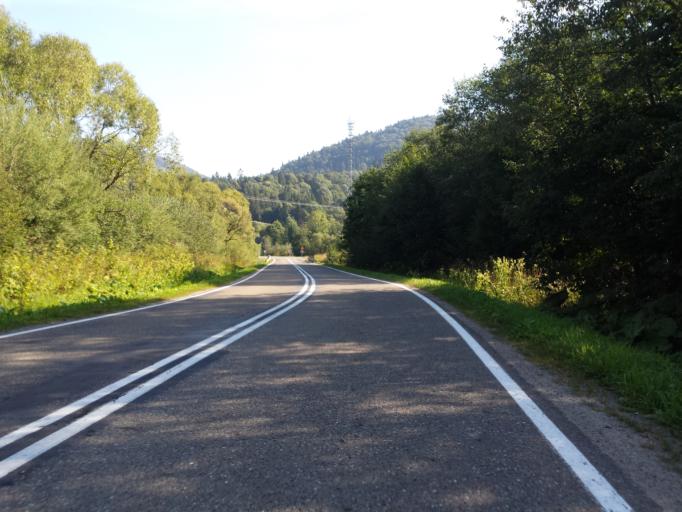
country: PL
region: Subcarpathian Voivodeship
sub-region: Powiat leski
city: Baligrod
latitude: 49.2665
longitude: 22.2875
